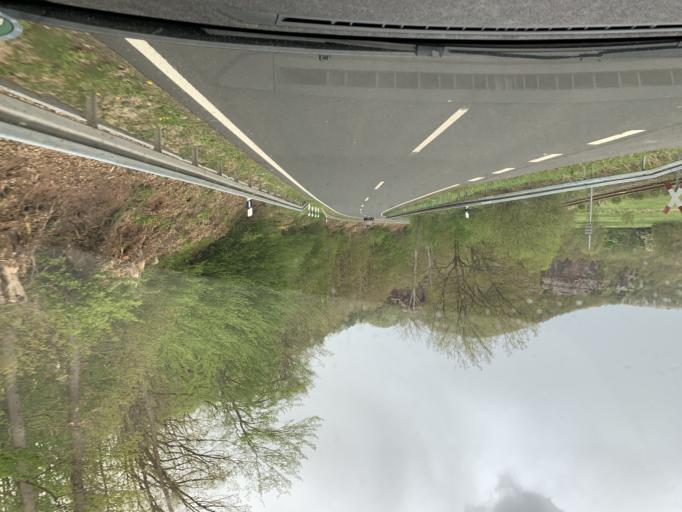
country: DE
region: North Rhine-Westphalia
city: Heimbach
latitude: 50.6567
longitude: 6.4969
